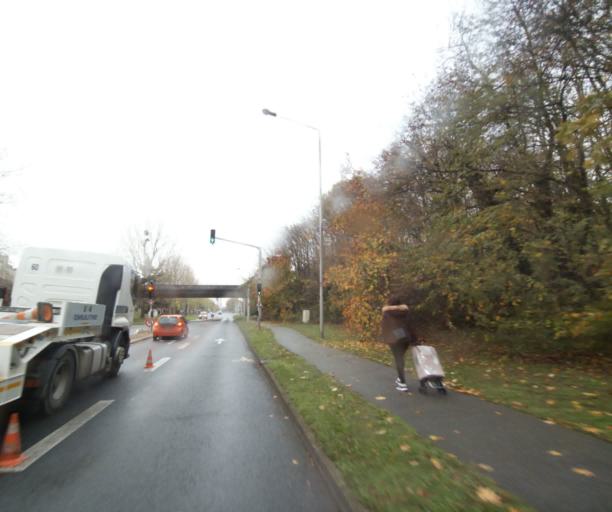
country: FR
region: Ile-de-France
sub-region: Departement de l'Essonne
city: Ris-Orangis
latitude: 48.6336
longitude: 2.4252
